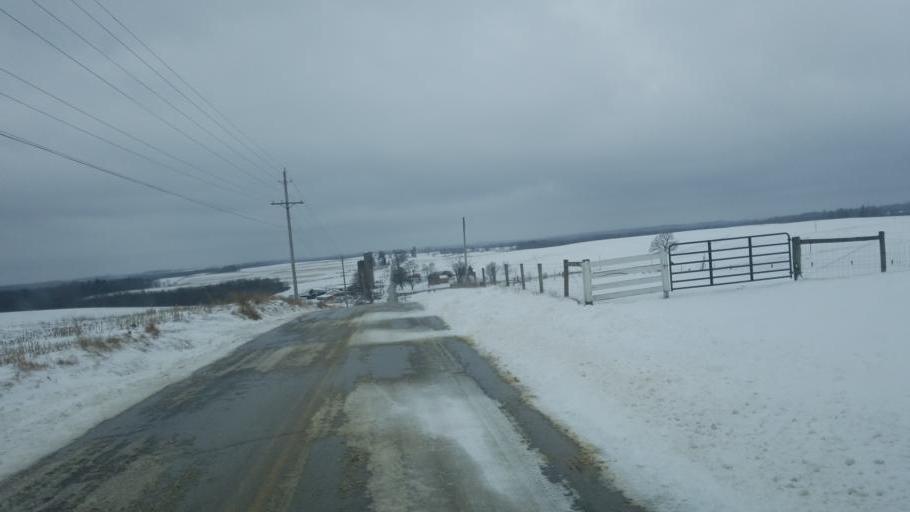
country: US
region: Ohio
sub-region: Knox County
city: Oak Hill
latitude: 40.4722
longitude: -82.1292
